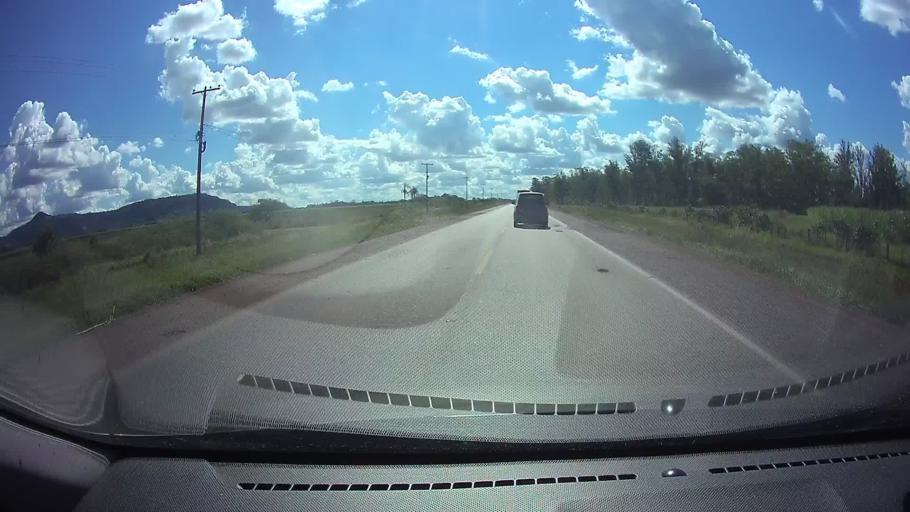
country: PY
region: Paraguari
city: La Colmena
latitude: -25.7557
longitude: -56.7673
